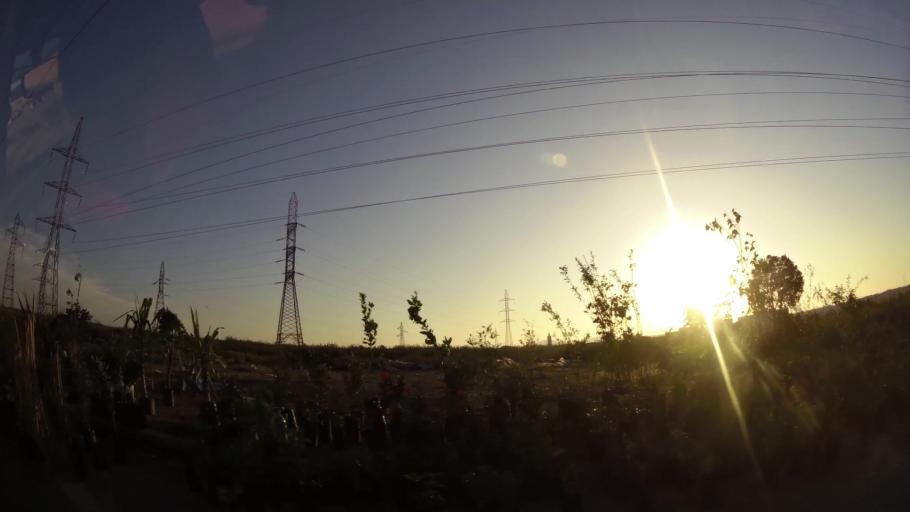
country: MA
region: Oriental
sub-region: Oujda-Angad
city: Oujda
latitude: 34.7103
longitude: -1.9161
